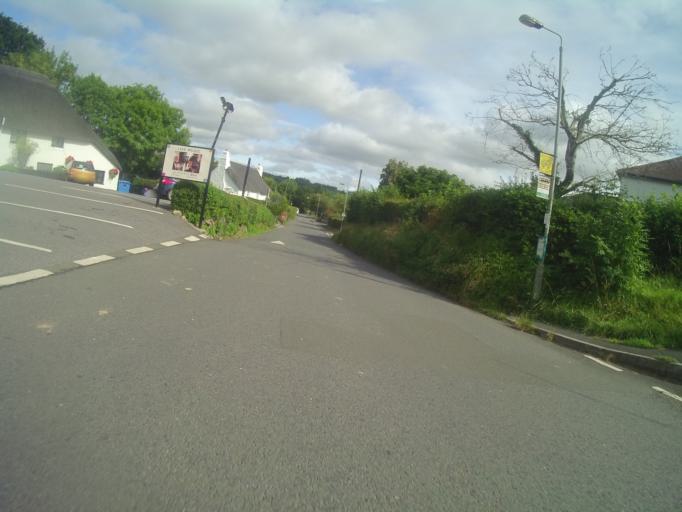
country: GB
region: England
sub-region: Devon
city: Totnes
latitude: 50.4421
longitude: -3.7081
